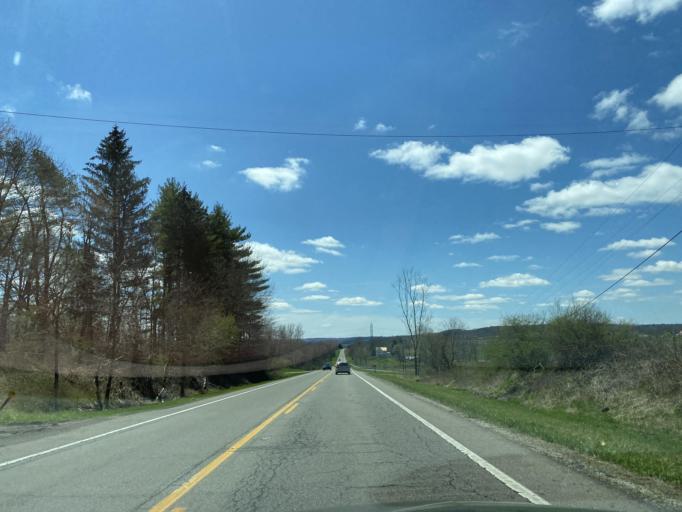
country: US
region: Ohio
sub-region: Wayne County
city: Shreve
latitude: 40.7345
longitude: -81.9914
